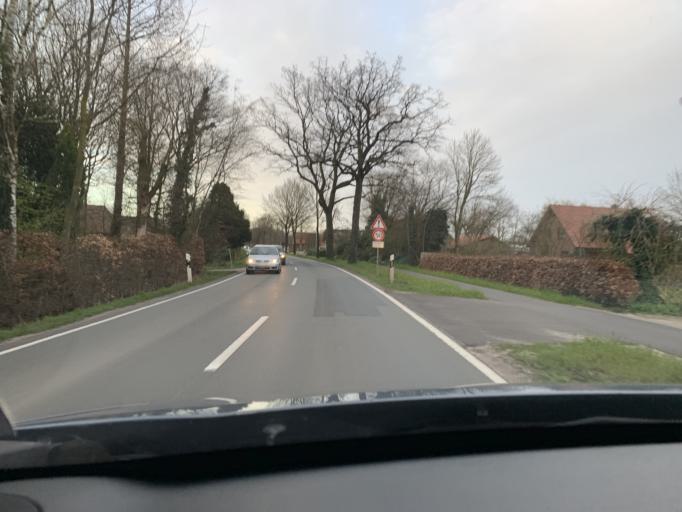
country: DE
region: Lower Saxony
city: Apen
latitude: 53.1913
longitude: 7.8666
